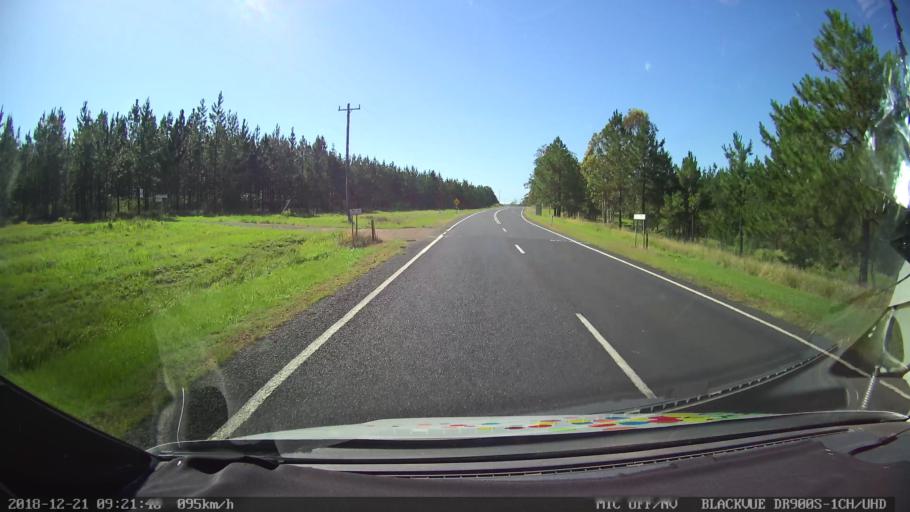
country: AU
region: New South Wales
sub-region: Clarence Valley
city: Maclean
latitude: -29.3320
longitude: 152.9993
